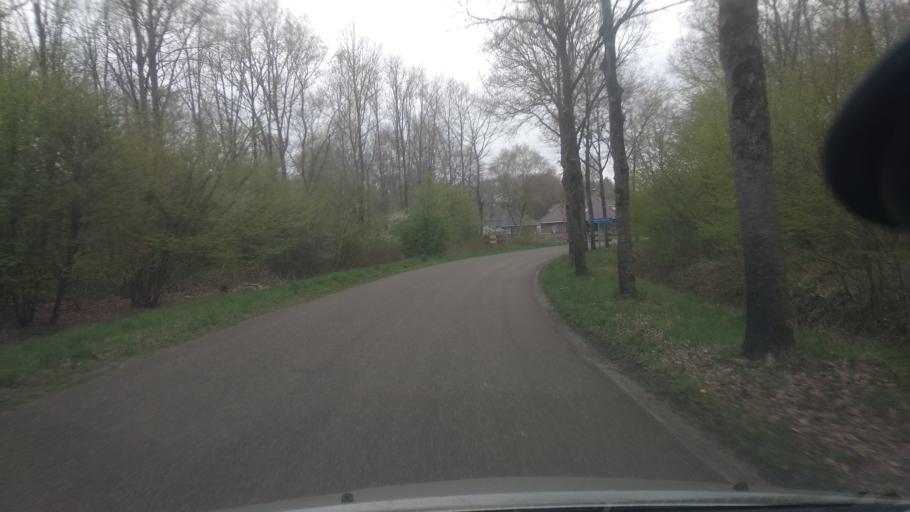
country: NL
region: Drenthe
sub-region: Gemeente Emmen
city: Emmer-Compascuum
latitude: 52.9035
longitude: 7.0131
